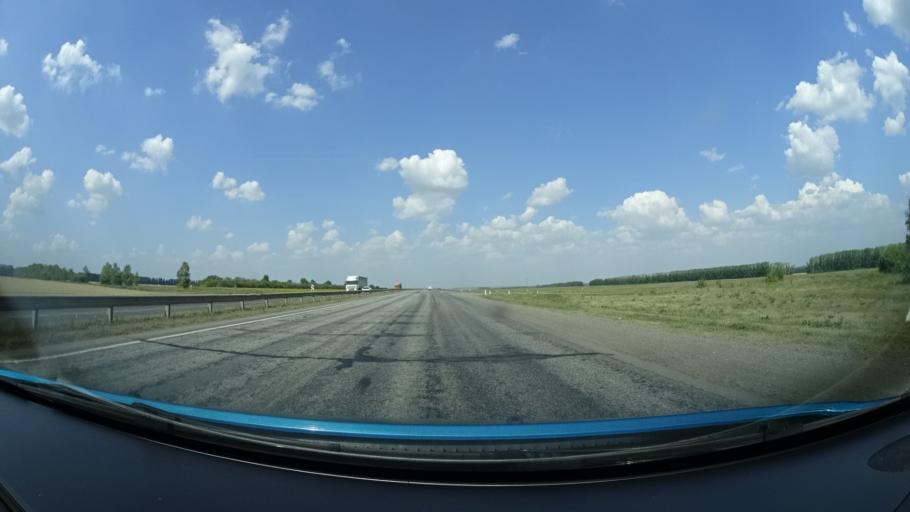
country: RU
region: Bashkortostan
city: Dmitriyevka
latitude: 54.7047
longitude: 55.2410
